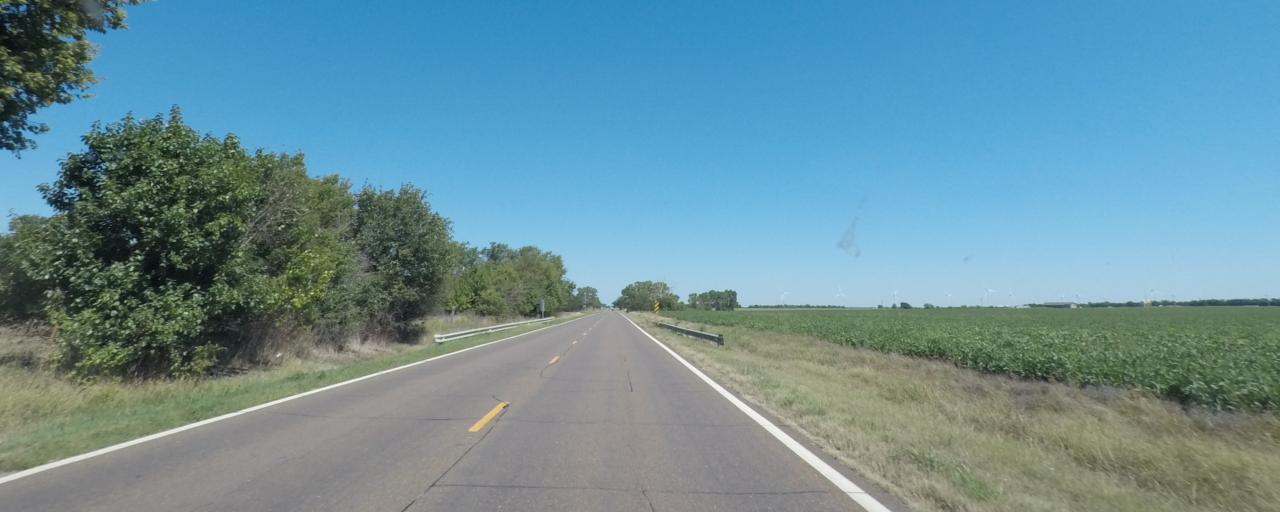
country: US
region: Kansas
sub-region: Sumner County
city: Wellington
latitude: 37.1103
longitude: -97.4016
